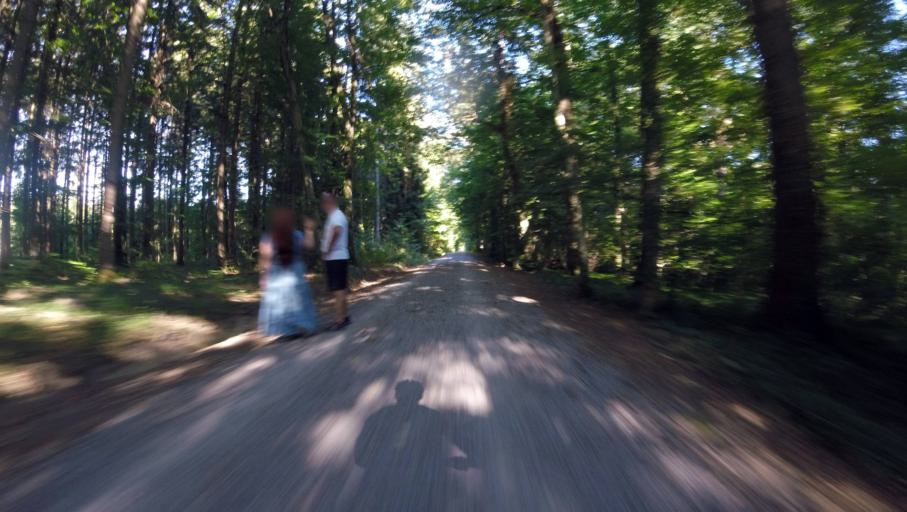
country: DE
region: Baden-Wuerttemberg
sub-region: Regierungsbezirk Stuttgart
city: Aspach
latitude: 48.9708
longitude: 9.3653
